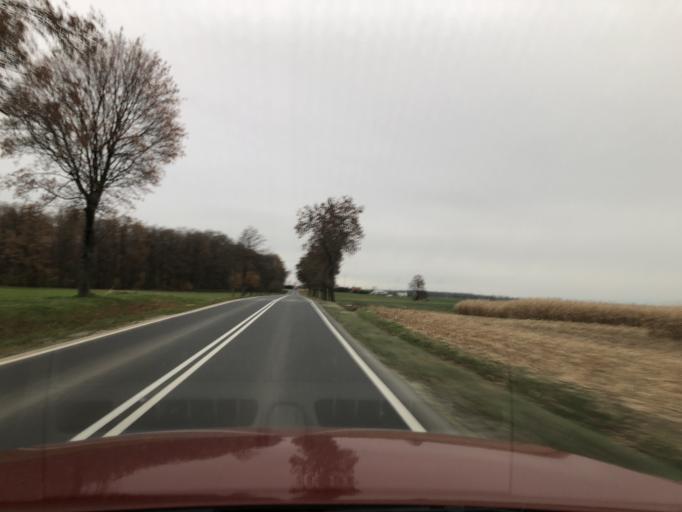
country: PL
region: Lower Silesian Voivodeship
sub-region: Powiat swidnicki
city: Zarow
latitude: 50.9781
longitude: 16.4961
